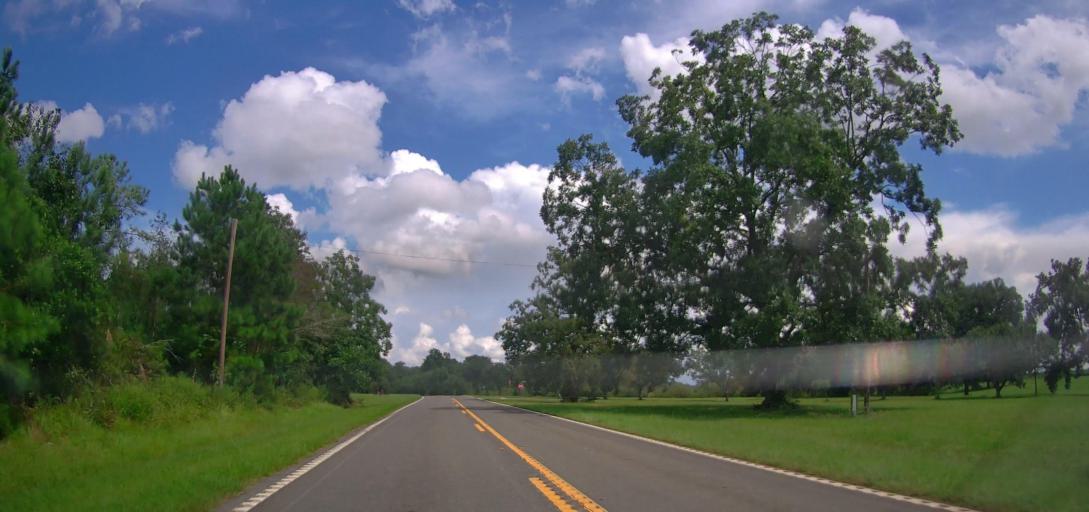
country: US
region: Georgia
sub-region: Taylor County
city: Reynolds
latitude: 32.4400
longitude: -84.1179
